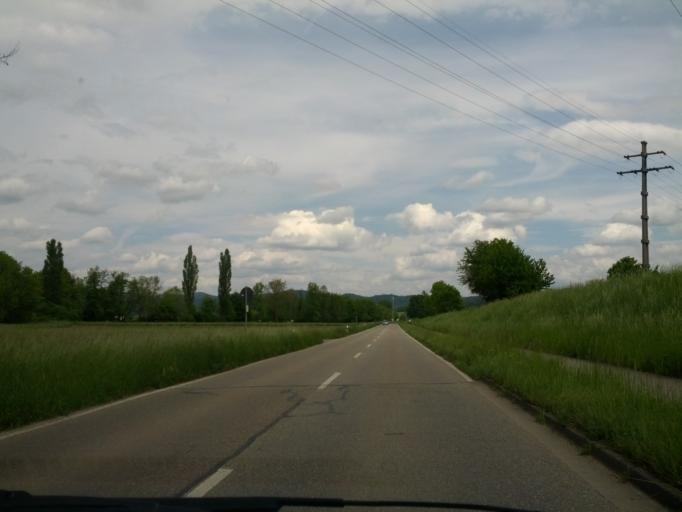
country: DE
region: Baden-Wuerttemberg
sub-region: Freiburg Region
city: Denzlingen
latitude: 48.0775
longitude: 7.8851
